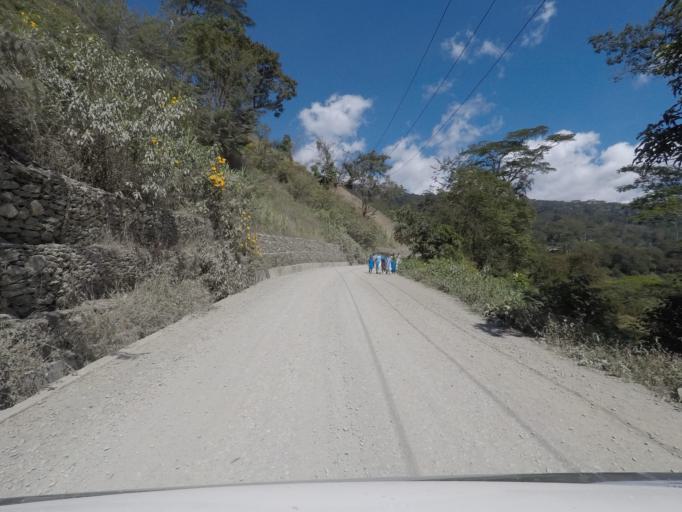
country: TL
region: Ermera
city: Gleno
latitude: -8.7457
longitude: 125.3908
